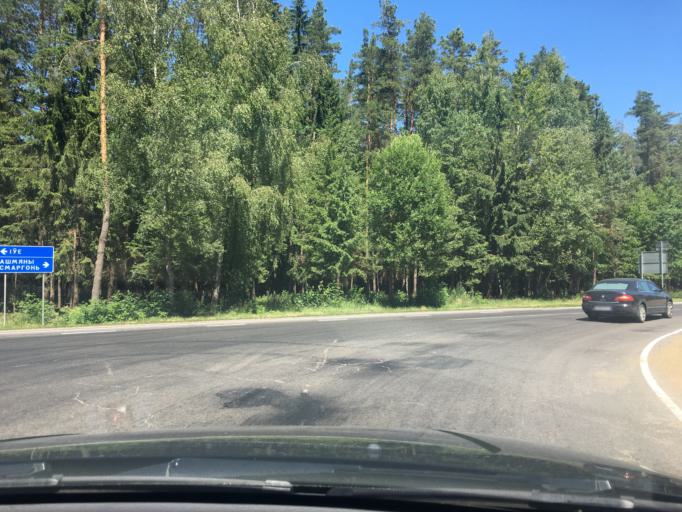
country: BY
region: Grodnenskaya
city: Iwye
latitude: 53.9419
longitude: 25.8098
